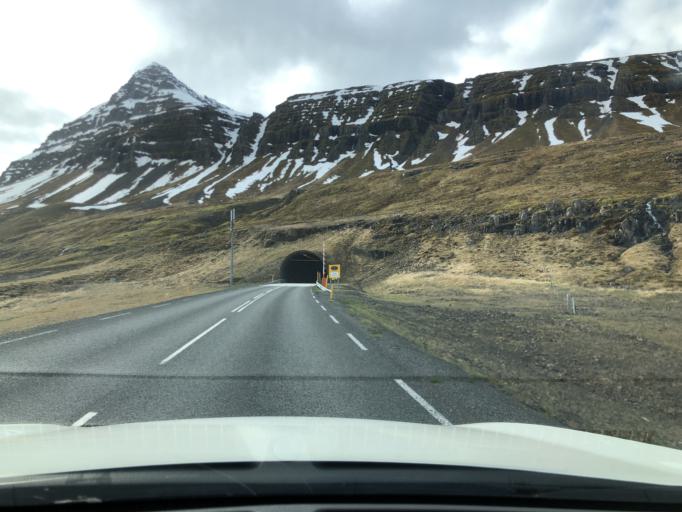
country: IS
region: East
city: Reydarfjoerdur
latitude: 65.0128
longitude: -14.1998
